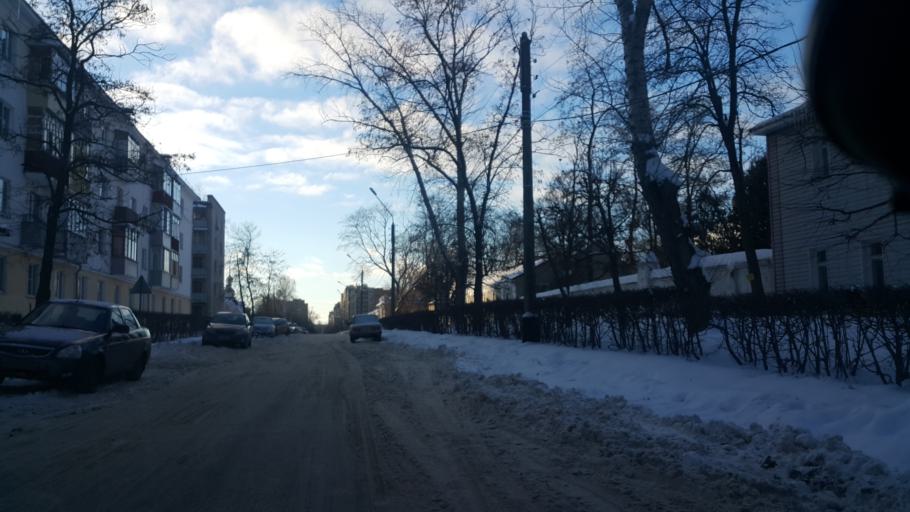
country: RU
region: Tambov
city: Tambov
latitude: 52.7058
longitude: 41.4799
